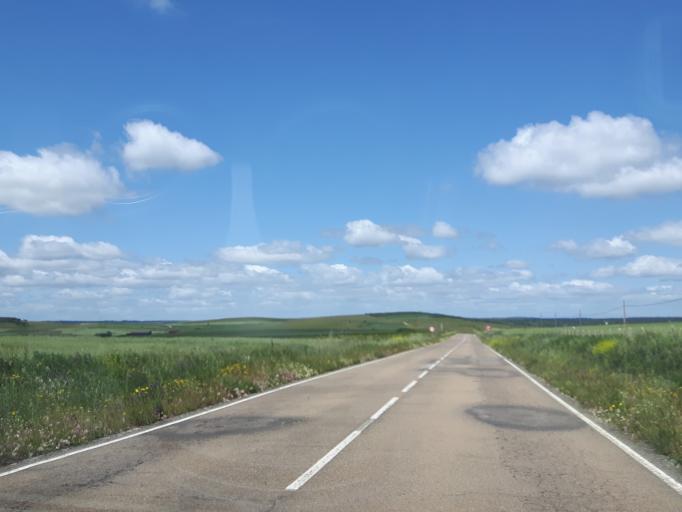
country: ES
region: Castille and Leon
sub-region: Provincia de Salamanca
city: Villar de la Yegua
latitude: 40.7314
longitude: -6.7210
